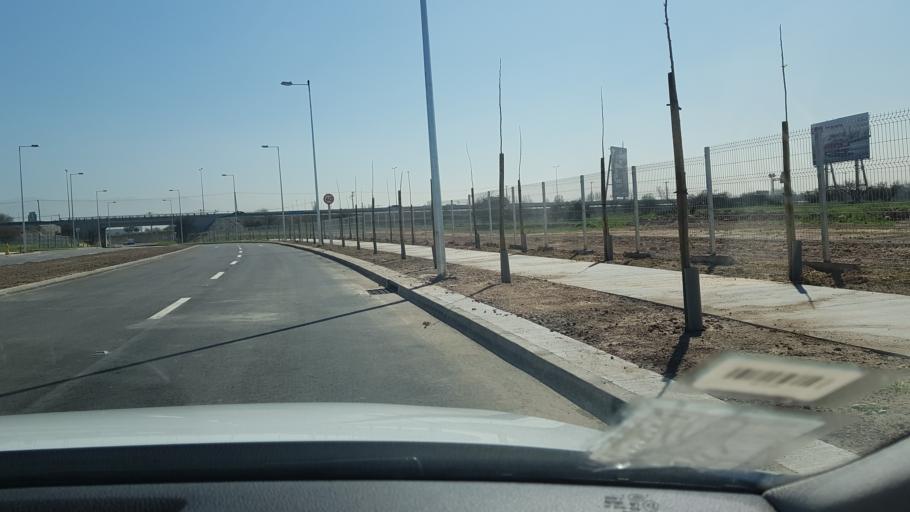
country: CL
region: Santiago Metropolitan
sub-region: Provincia de Santiago
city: Lo Prado
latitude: -33.4184
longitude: -70.7882
